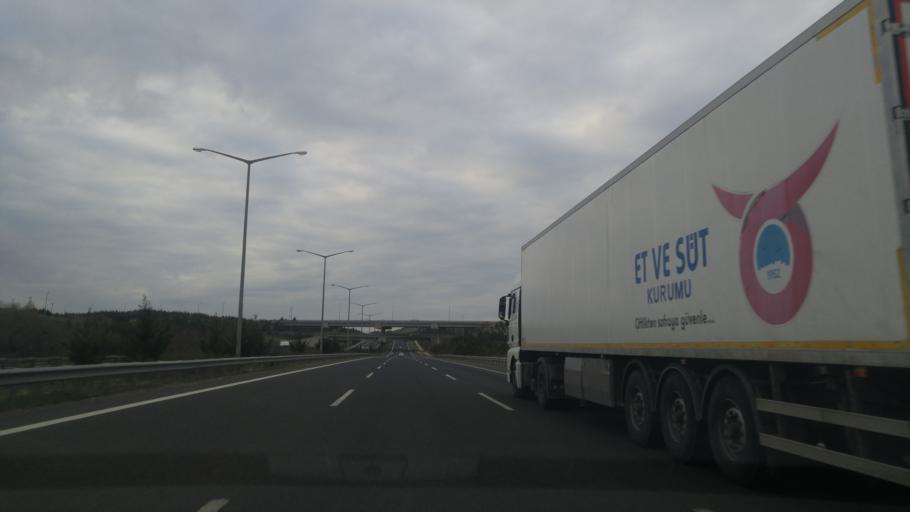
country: TR
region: Ankara
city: Etimesgut
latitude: 40.0121
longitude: 32.6289
